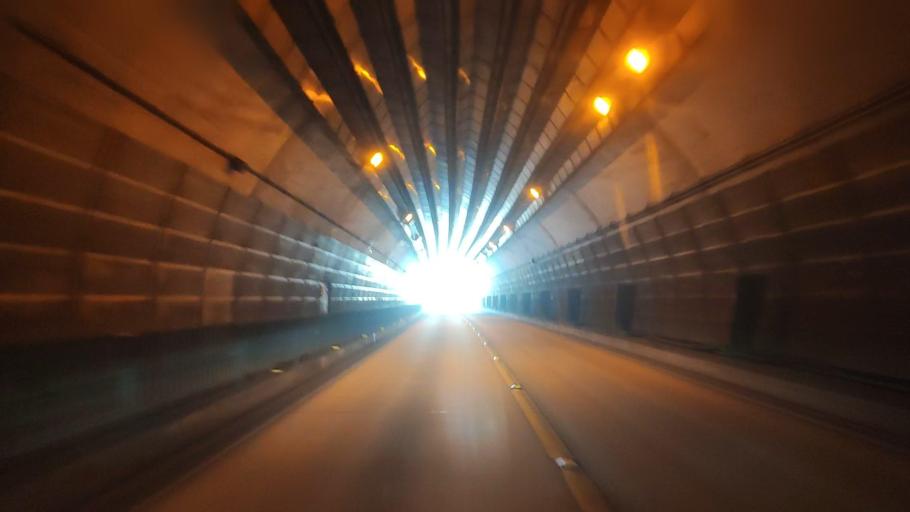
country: JP
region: Nara
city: Yoshino-cho
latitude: 34.3334
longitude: 135.9578
